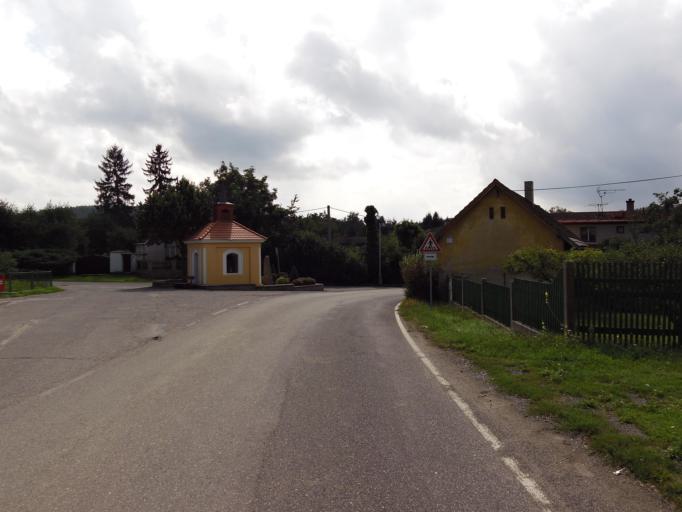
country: CZ
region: Central Bohemia
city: Kamenny Privoz
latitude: 49.8619
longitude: 14.4918
